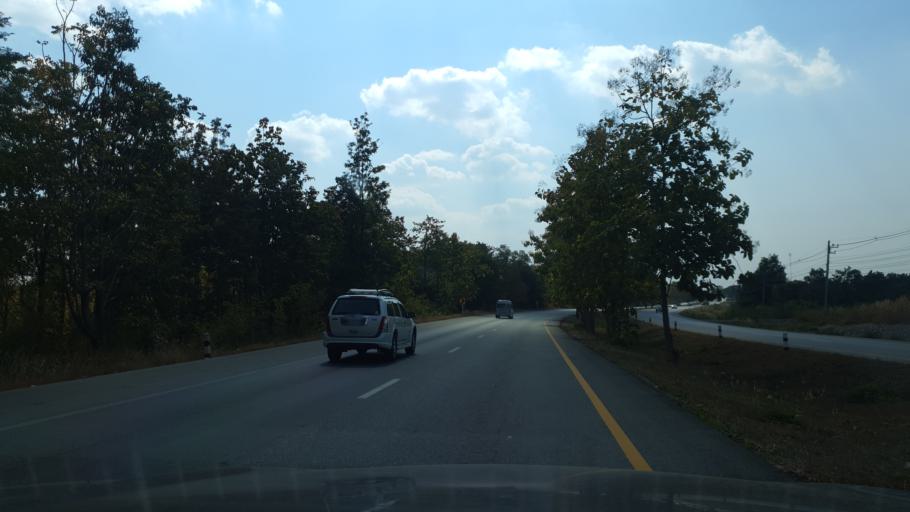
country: TH
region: Tak
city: Sam Ngao
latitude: 17.3044
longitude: 99.1476
